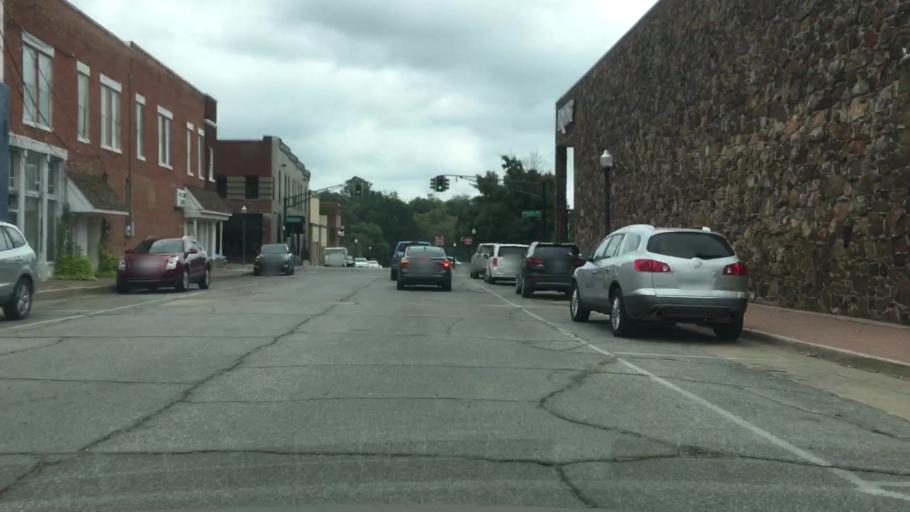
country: US
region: Oklahoma
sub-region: Cherokee County
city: Tahlequah
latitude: 35.9135
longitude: -94.9716
